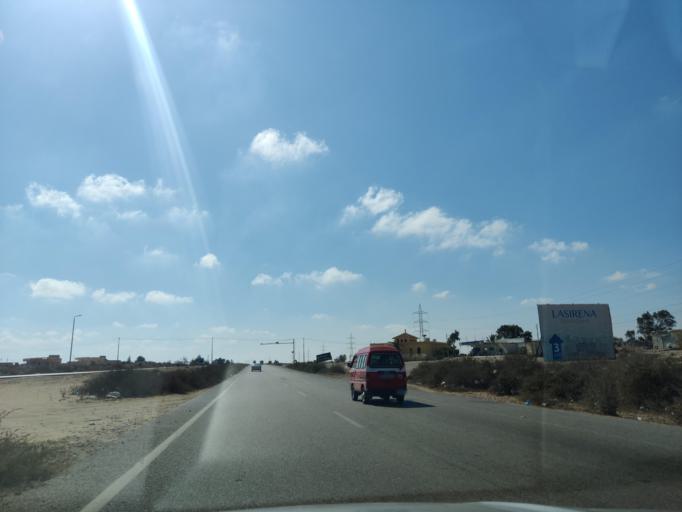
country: EG
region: Muhafazat Matruh
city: Al `Alamayn
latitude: 31.0452
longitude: 28.3445
